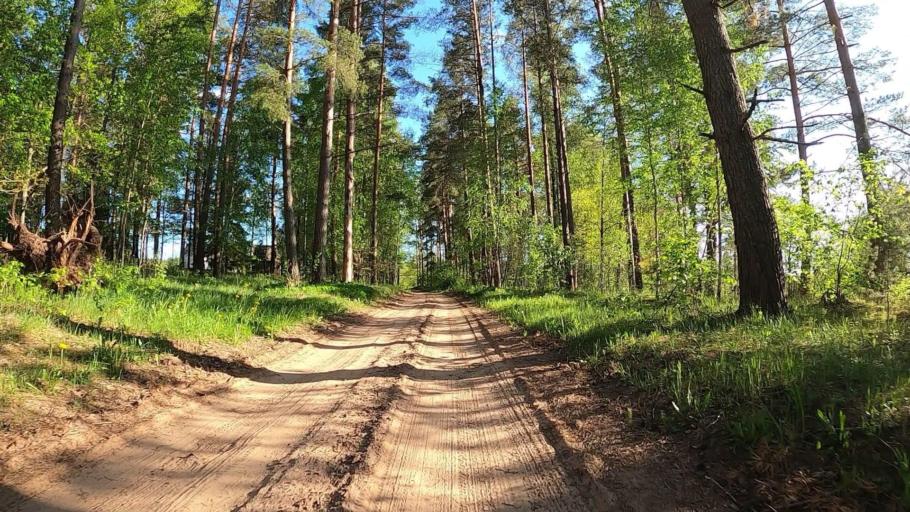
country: LV
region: Baldone
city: Baldone
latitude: 56.7731
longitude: 24.3351
